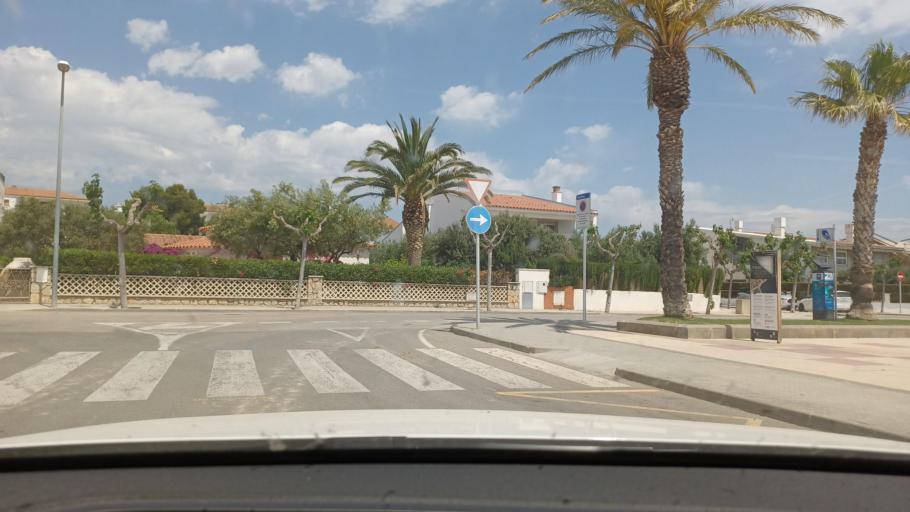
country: ES
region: Catalonia
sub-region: Provincia de Tarragona
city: Colldejou
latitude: 40.9907
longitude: 0.9291
